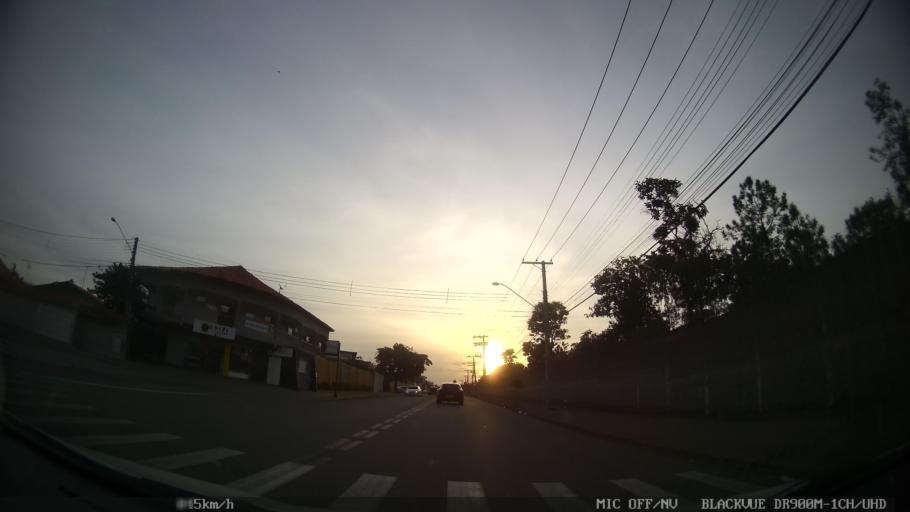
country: BR
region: Sao Paulo
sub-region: Limeira
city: Limeira
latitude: -22.5799
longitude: -47.4195
